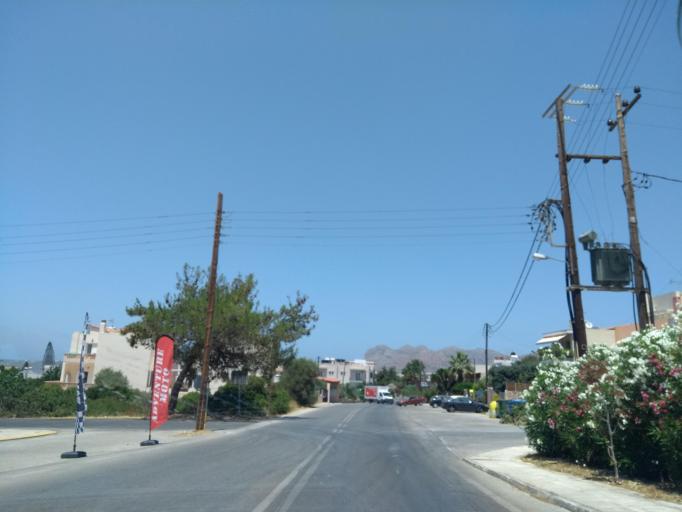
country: GR
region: Crete
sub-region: Nomos Chanias
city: Pithari
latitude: 35.5466
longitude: 24.0825
